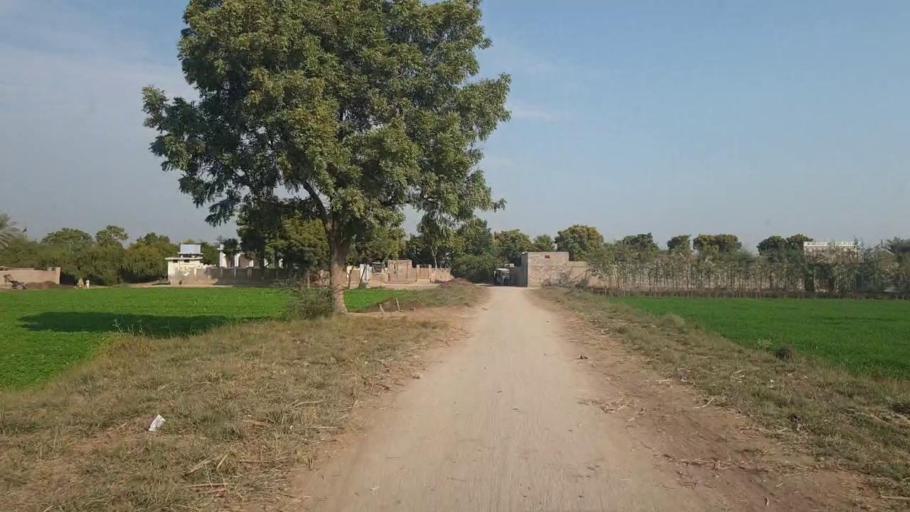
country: PK
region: Sindh
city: Tando Adam
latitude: 25.7533
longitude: 68.5991
